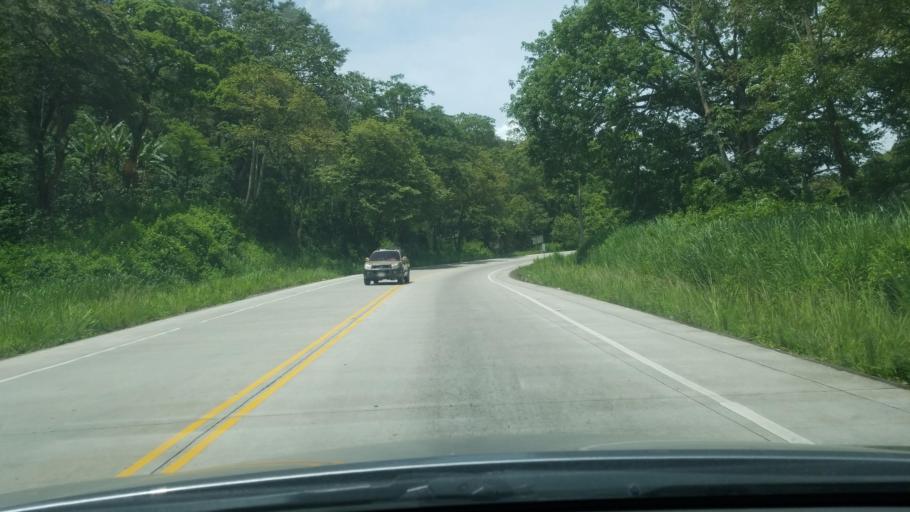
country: HN
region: Copan
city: Agua Caliente
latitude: 14.8685
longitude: -88.7851
